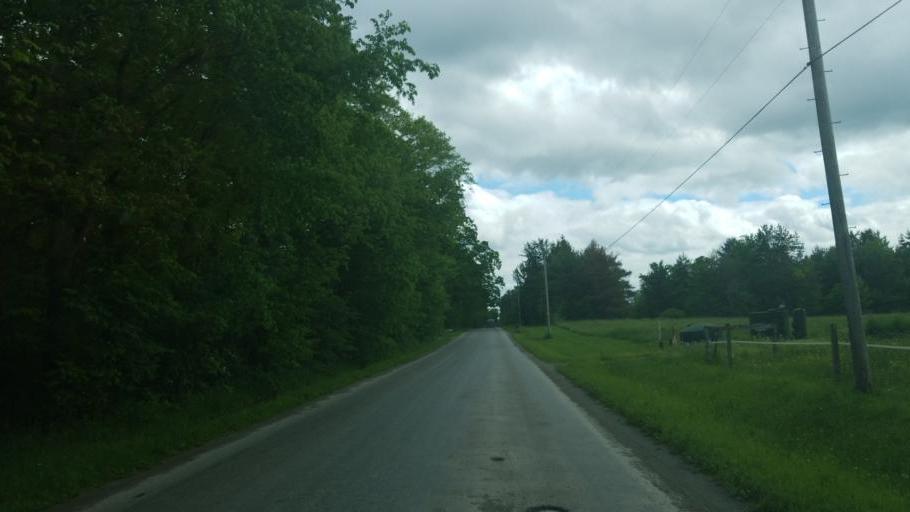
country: US
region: Ohio
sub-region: Geauga County
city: Middlefield
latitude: 41.4441
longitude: -81.0034
